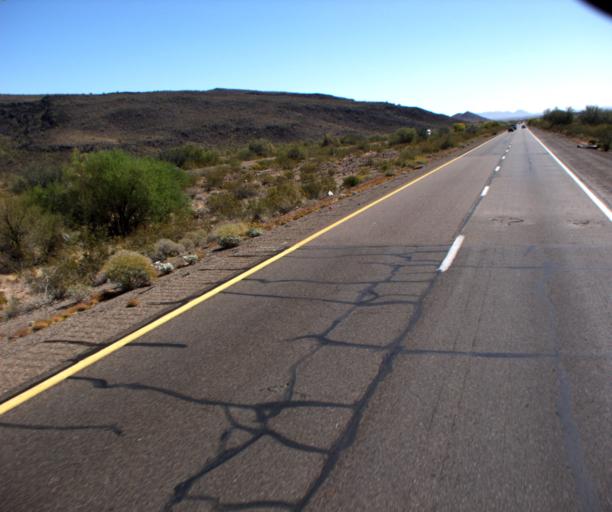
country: US
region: Arizona
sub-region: La Paz County
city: Quartzsite
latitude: 33.6499
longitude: -113.9145
